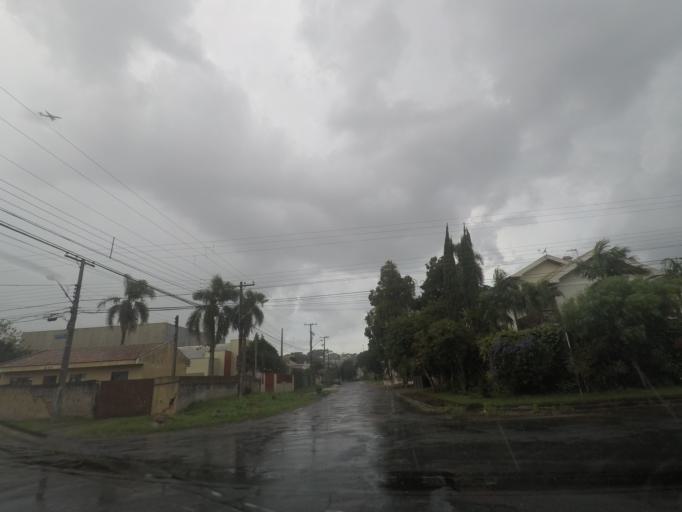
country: BR
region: Parana
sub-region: Curitiba
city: Curitiba
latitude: -25.4747
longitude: -49.2453
